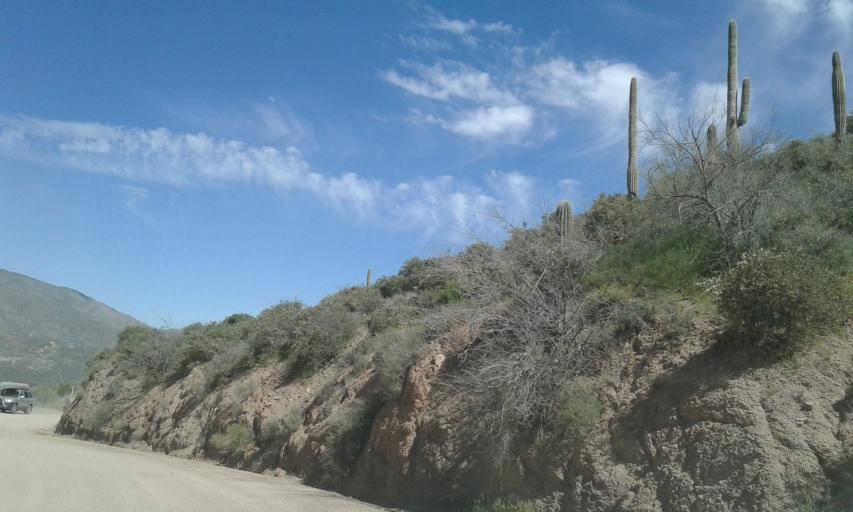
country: US
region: Arizona
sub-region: Pinal County
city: Gold Camp
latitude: 33.5515
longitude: -111.2535
